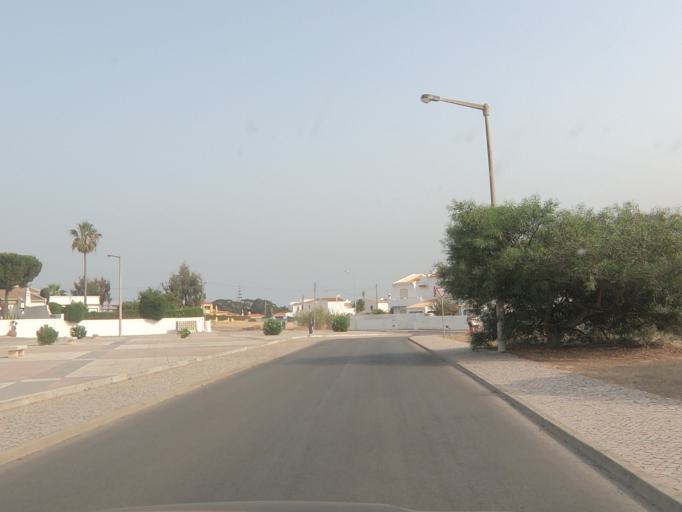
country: PT
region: Faro
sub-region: Albufeira
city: Guia
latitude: 37.0807
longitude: -8.3072
